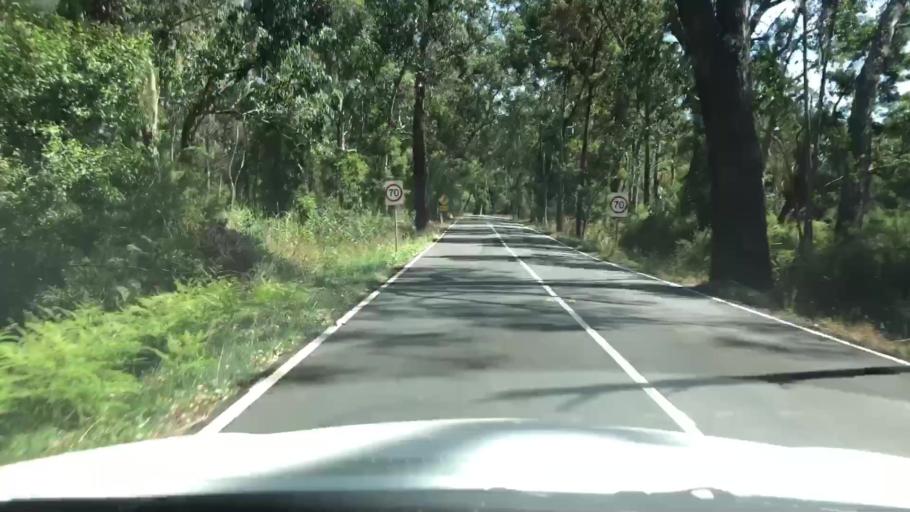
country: AU
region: Victoria
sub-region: Yarra Ranges
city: Woori Yallock
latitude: -37.8141
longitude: 145.5024
